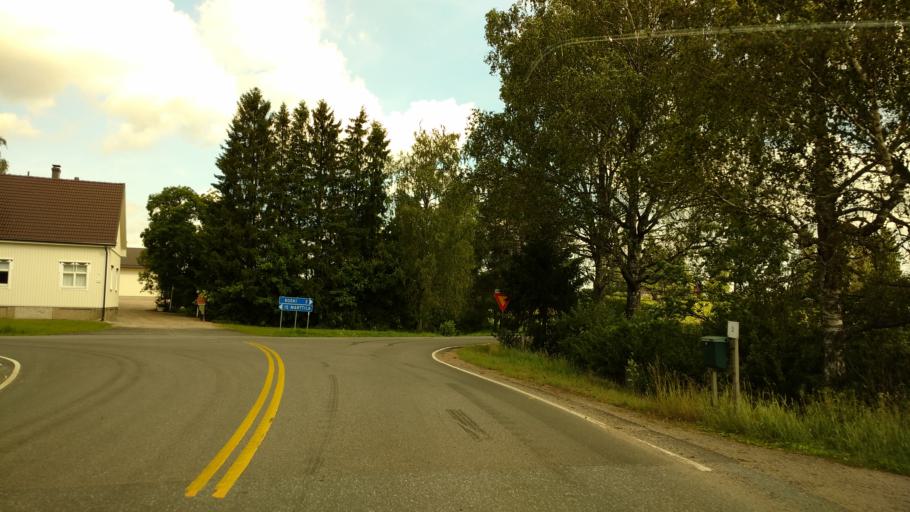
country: FI
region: Varsinais-Suomi
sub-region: Loimaa
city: Koski Tl
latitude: 60.6404
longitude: 23.1075
